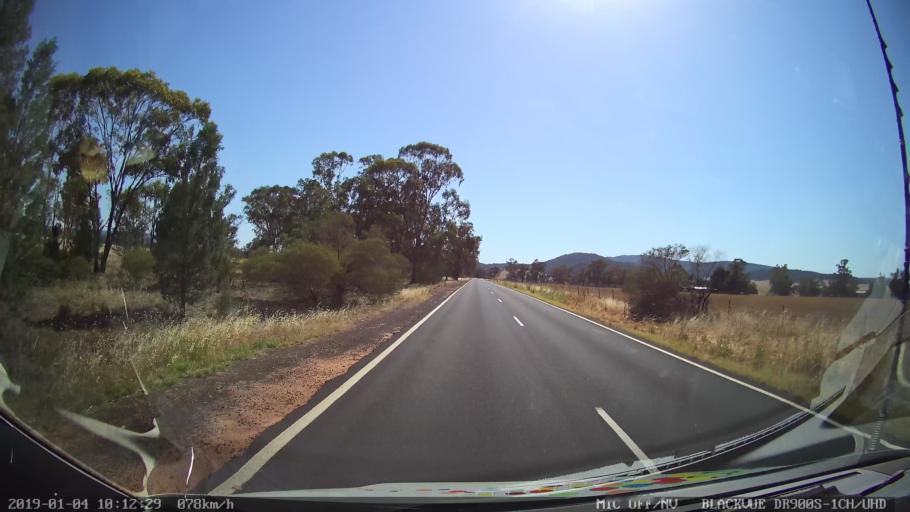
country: AU
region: New South Wales
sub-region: Cabonne
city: Canowindra
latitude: -33.4126
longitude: 148.3952
